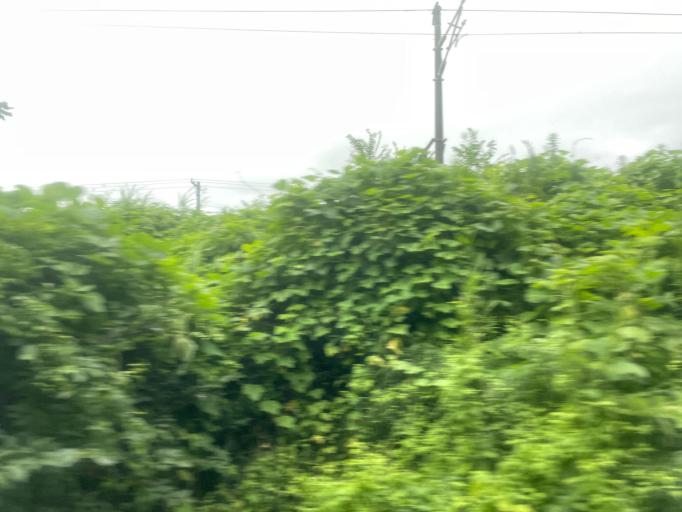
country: JP
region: Fukushima
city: Nihommatsu
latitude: 37.5563
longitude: 140.4063
